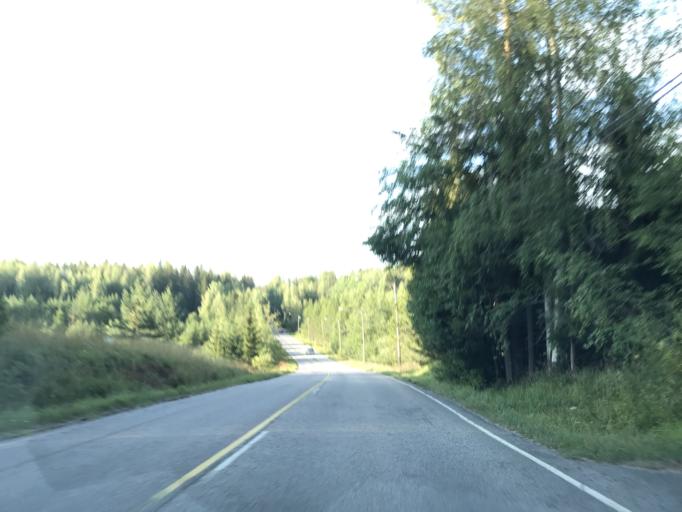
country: FI
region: Uusimaa
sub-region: Helsinki
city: Kauniainen
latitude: 60.3321
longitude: 24.7094
